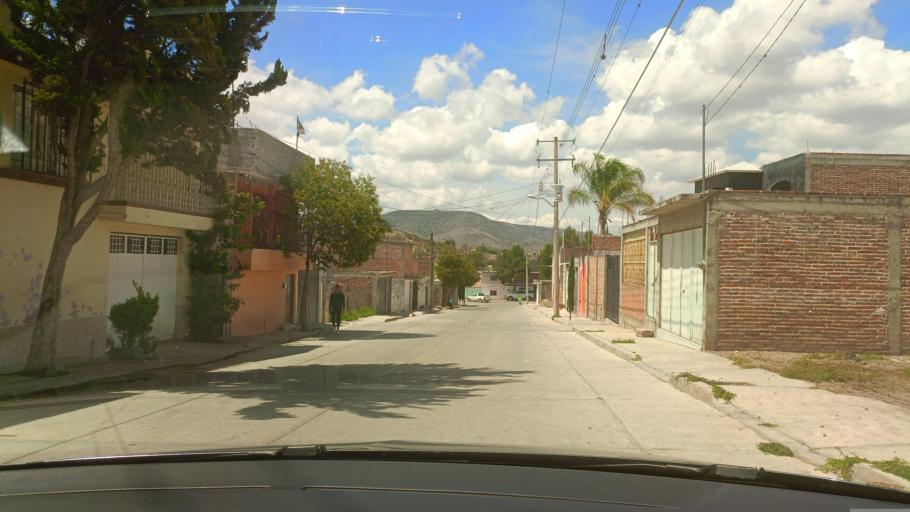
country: MX
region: Guanajuato
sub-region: San Luis de la Paz
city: San Luis de la Paz
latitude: 21.3033
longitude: -100.5071
